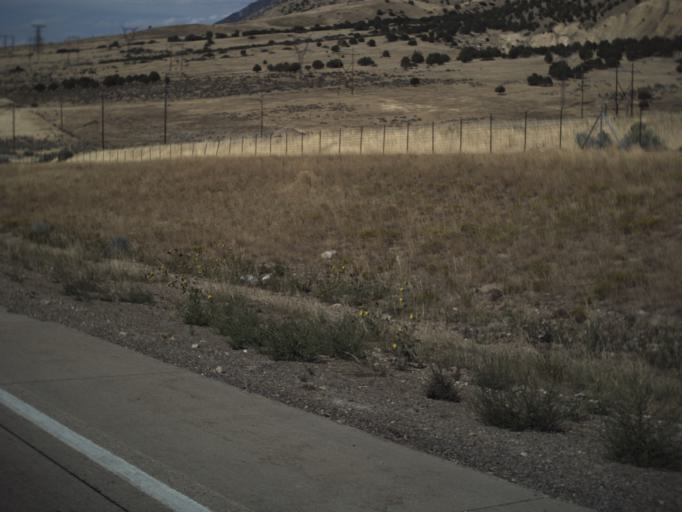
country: US
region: Utah
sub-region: Juab County
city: Nephi
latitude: 39.7531
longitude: -111.8343
